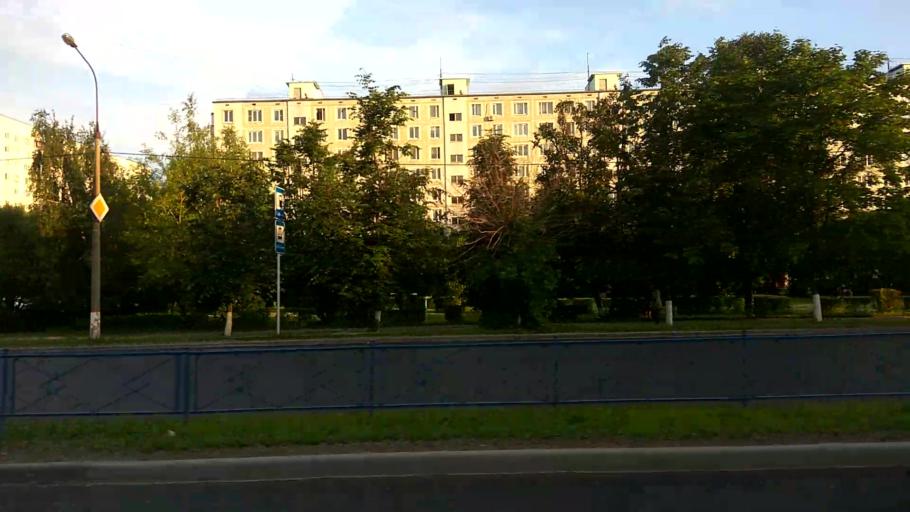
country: RU
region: Moskovskaya
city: Yubileyny
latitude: 55.9132
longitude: 37.8618
